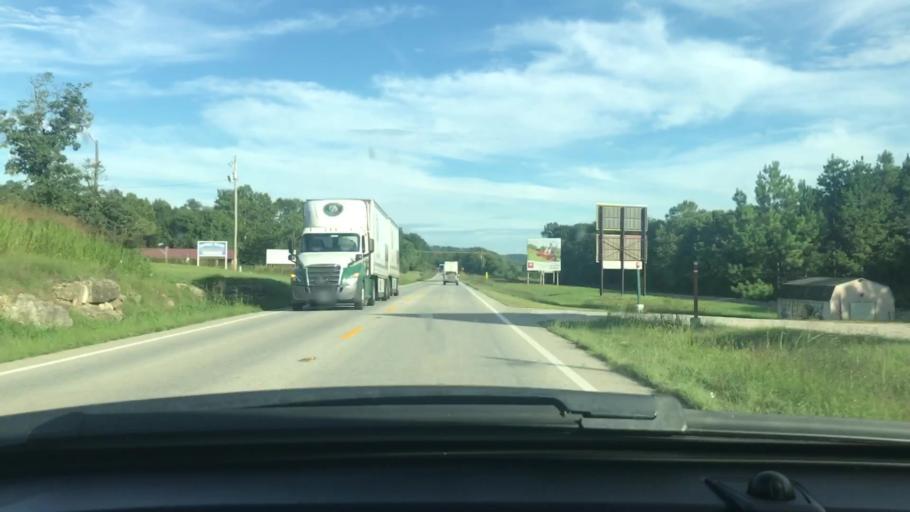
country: US
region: Arkansas
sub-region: Sharp County
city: Cherokee Village
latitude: 36.3006
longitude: -91.4421
